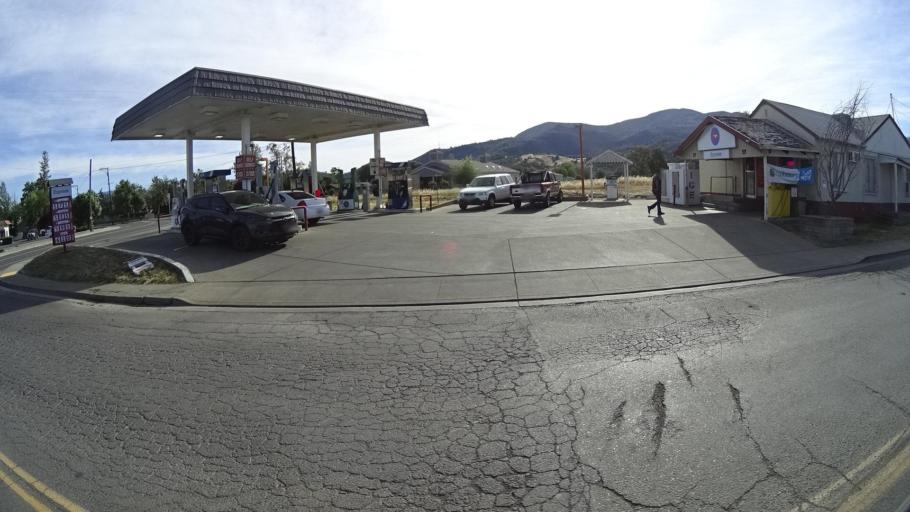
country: US
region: California
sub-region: Lake County
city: Kelseyville
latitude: 38.9772
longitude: -122.8341
